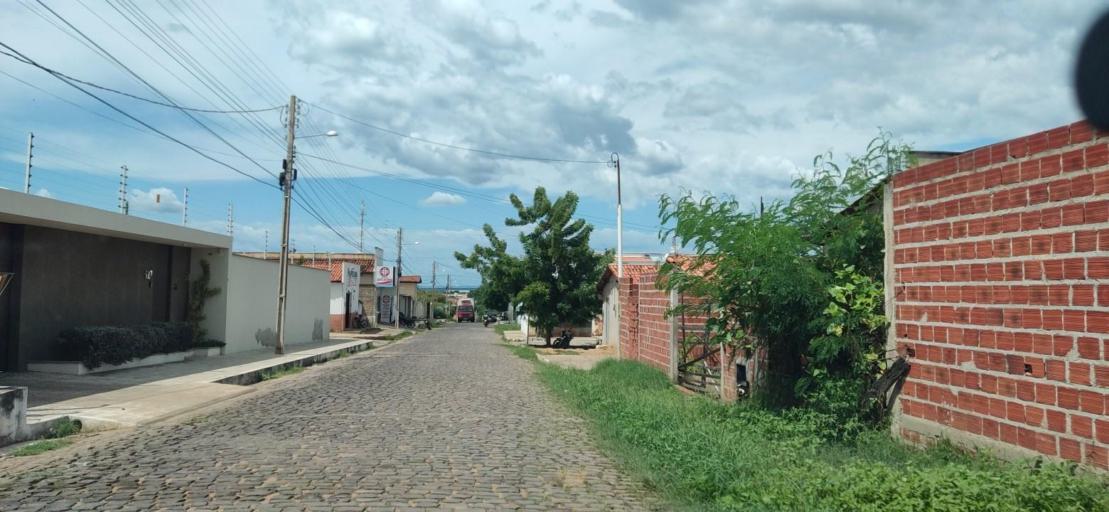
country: BR
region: Piaui
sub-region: Valenca Do Piaui
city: Valenca do Piaui
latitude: -6.4071
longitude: -41.7438
